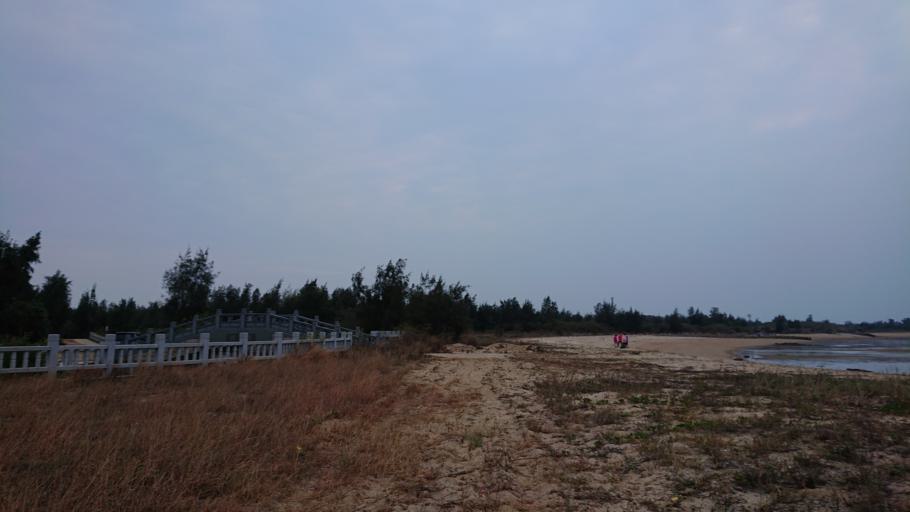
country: TW
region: Fukien
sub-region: Kinmen
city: Jincheng
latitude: 24.4287
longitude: 118.2267
